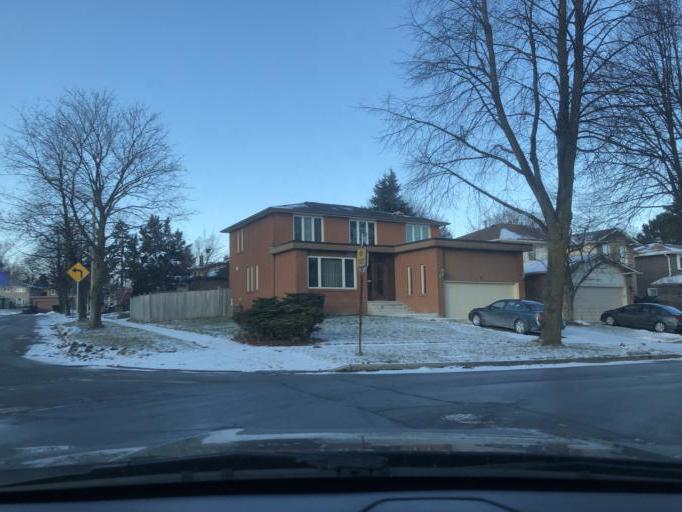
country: CA
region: Ontario
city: Scarborough
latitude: 43.7817
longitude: -79.1519
